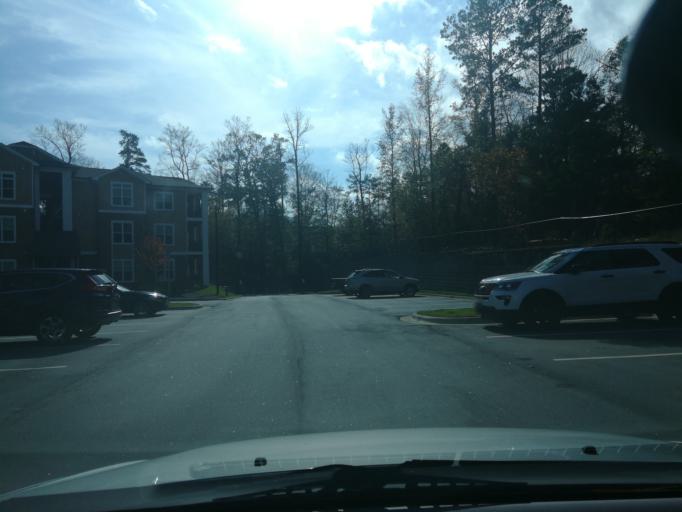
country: US
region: North Carolina
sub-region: Durham County
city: Durham
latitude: 36.0593
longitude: -78.9385
